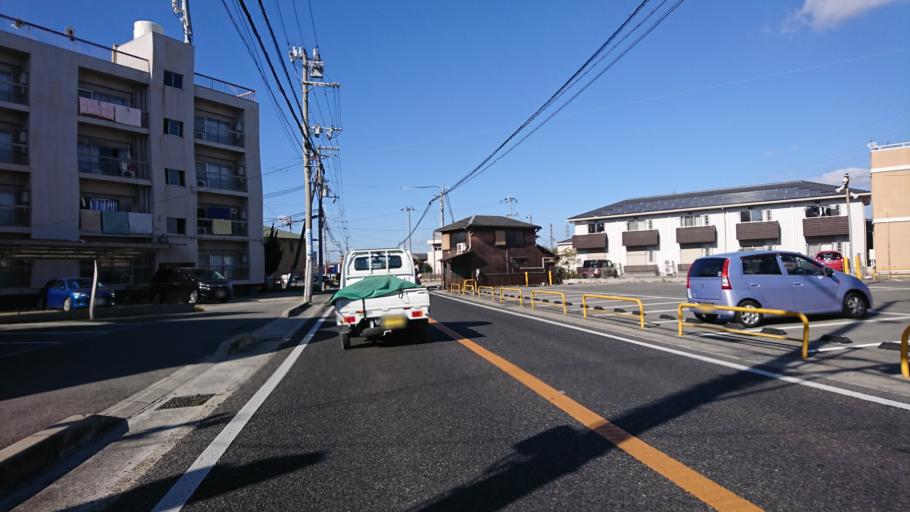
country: JP
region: Hyogo
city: Akashi
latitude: 34.6518
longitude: 134.9640
